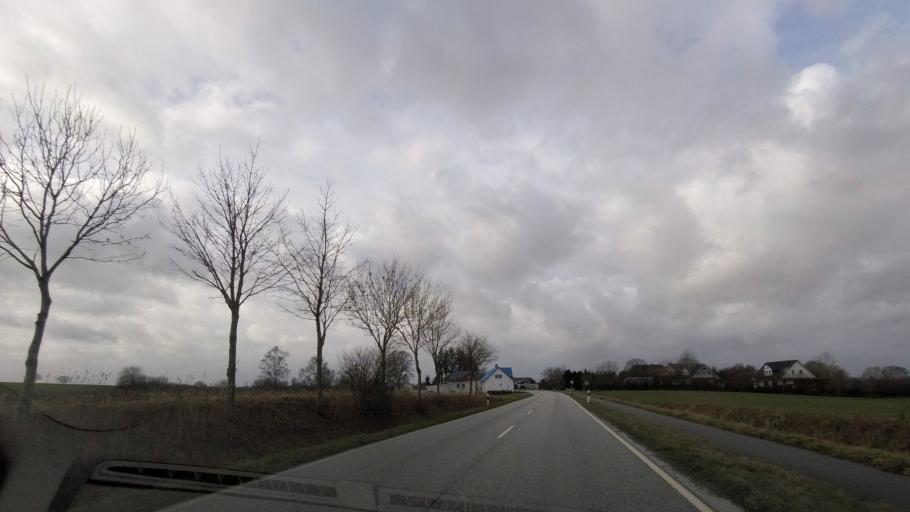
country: DE
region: Schleswig-Holstein
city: Dollrottfeld
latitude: 54.6434
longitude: 9.8219
